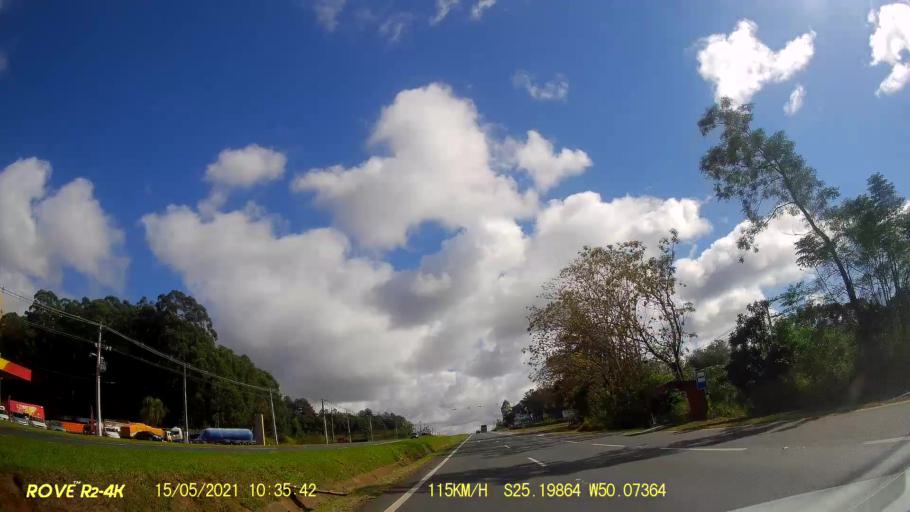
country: BR
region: Parana
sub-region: Ponta Grossa
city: Ponta Grossa
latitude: -25.1985
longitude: -50.0734
